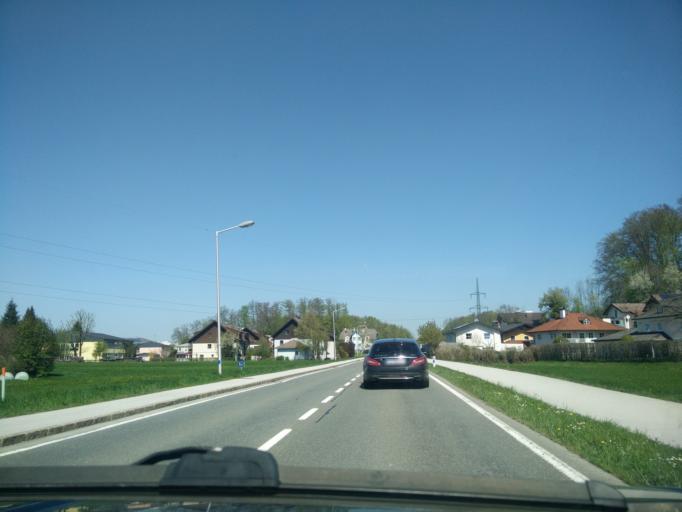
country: AT
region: Salzburg
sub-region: Politischer Bezirk Salzburg-Umgebung
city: Elsbethen
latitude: 47.7576
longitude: 13.0869
